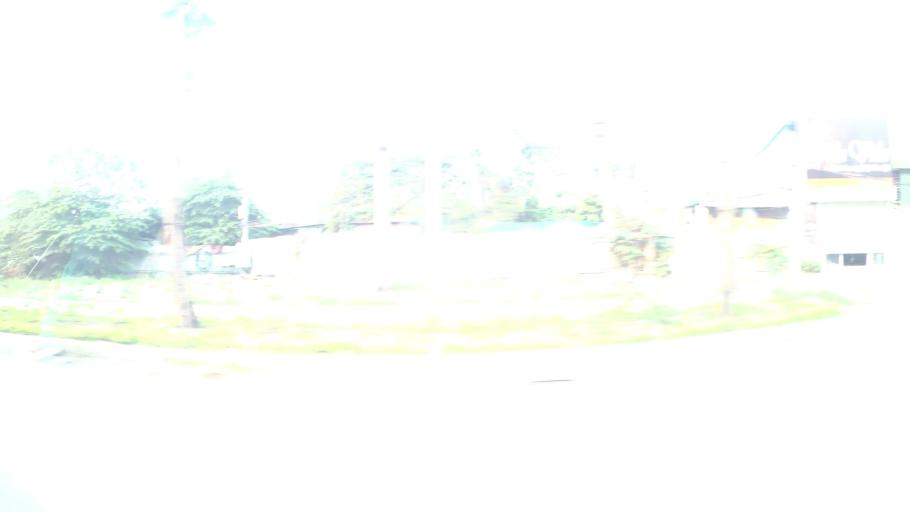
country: VN
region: Ha Noi
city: Thanh Xuan
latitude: 20.9761
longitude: 105.8175
